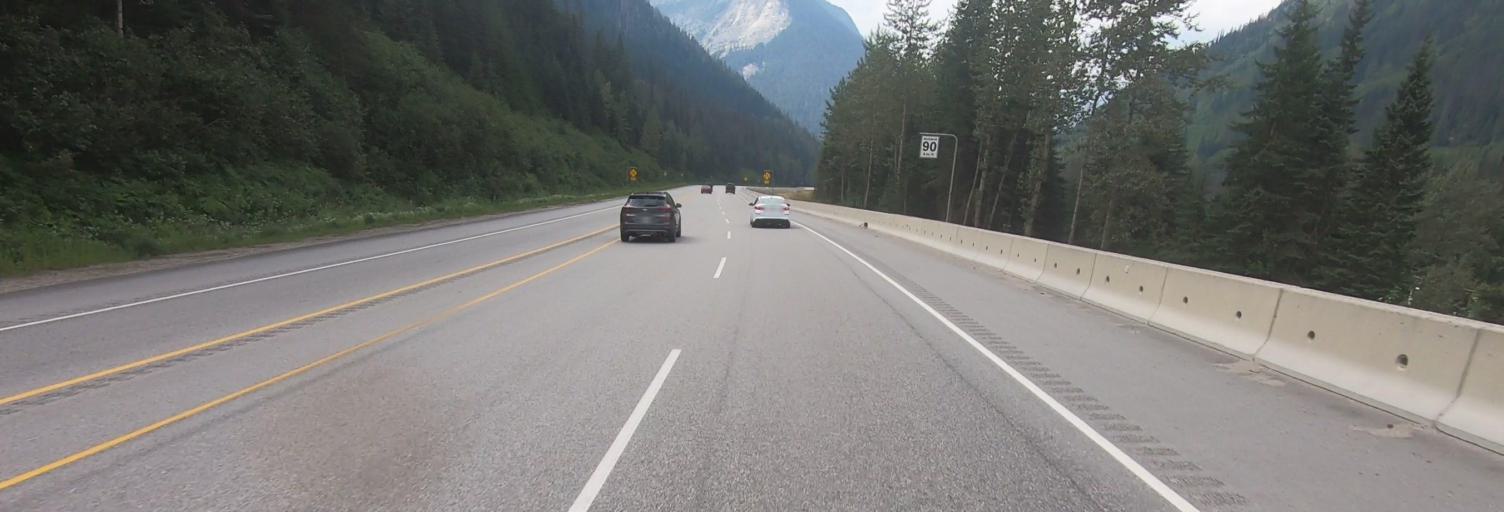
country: CA
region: British Columbia
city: Golden
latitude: 51.2679
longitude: -117.5122
